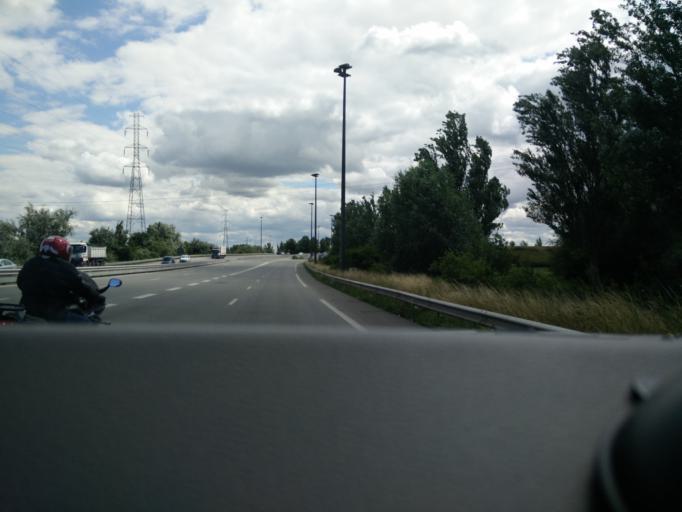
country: FR
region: Nord-Pas-de-Calais
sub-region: Departement du Nord
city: Coudekerque-Branche
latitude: 51.0249
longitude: 2.4086
